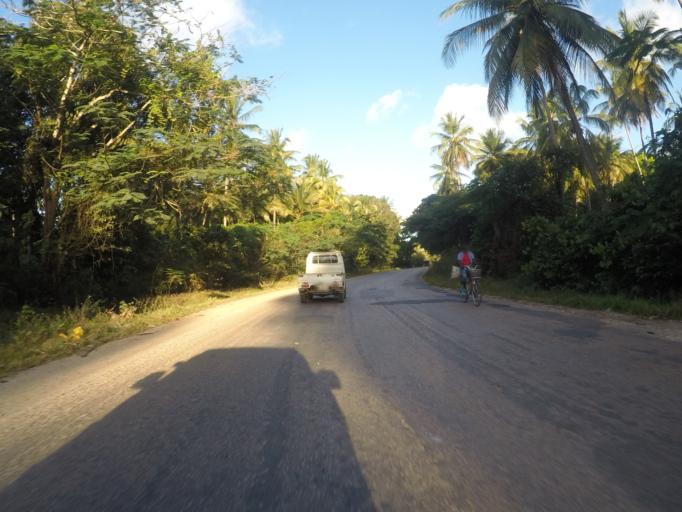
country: TZ
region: Zanzibar Central/South
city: Koani
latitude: -6.2016
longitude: 39.3193
